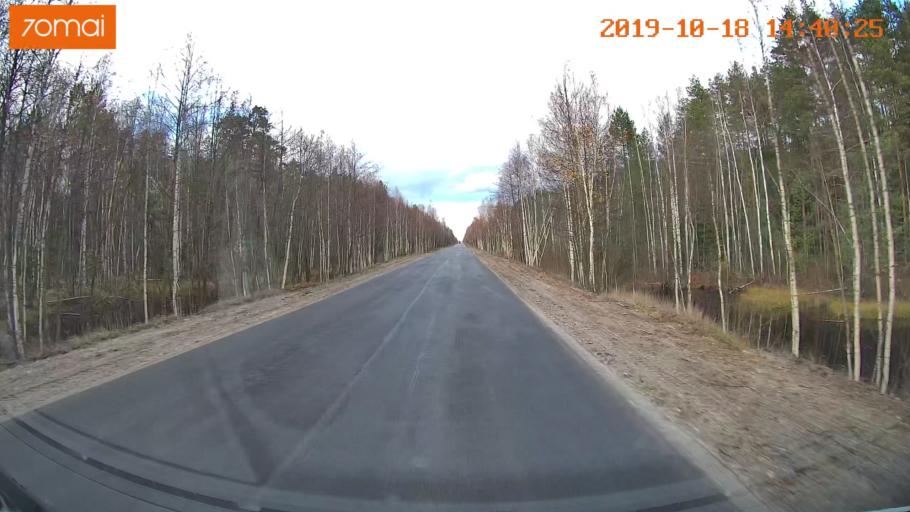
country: RU
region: Vladimir
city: Velikodvorskiy
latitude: 55.2763
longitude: 40.6689
